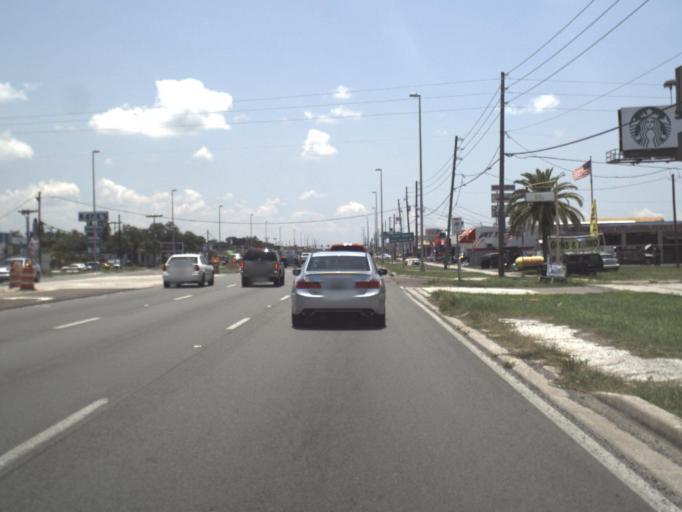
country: US
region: Florida
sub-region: Pasco County
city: New Port Richey
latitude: 28.2466
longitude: -82.7279
